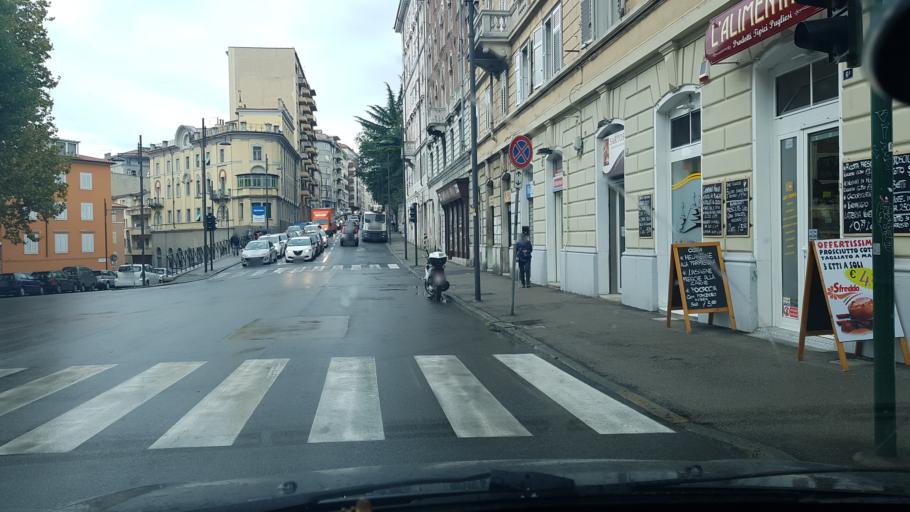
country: IT
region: Friuli Venezia Giulia
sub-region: Provincia di Trieste
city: Trieste
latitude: 45.6453
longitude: 13.7746
